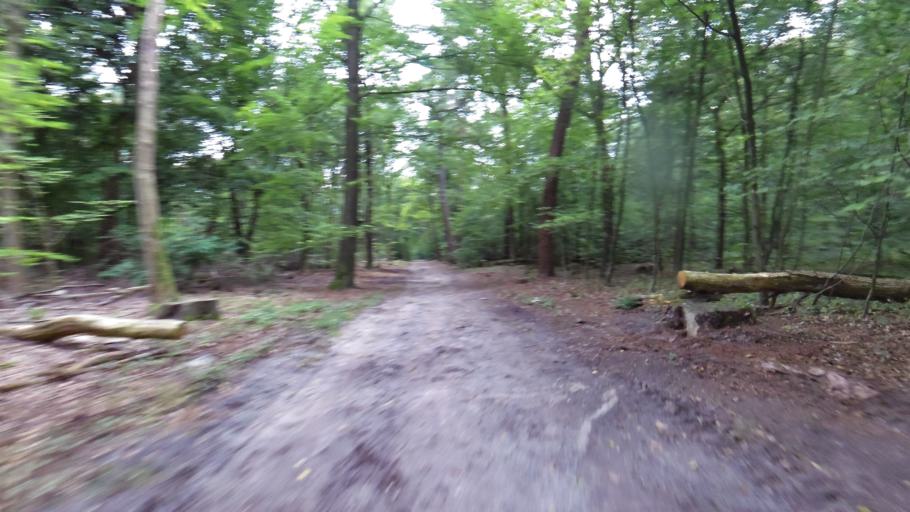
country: NL
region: Gelderland
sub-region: Gemeente Ede
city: Bennekom
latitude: 52.0018
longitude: 5.6966
